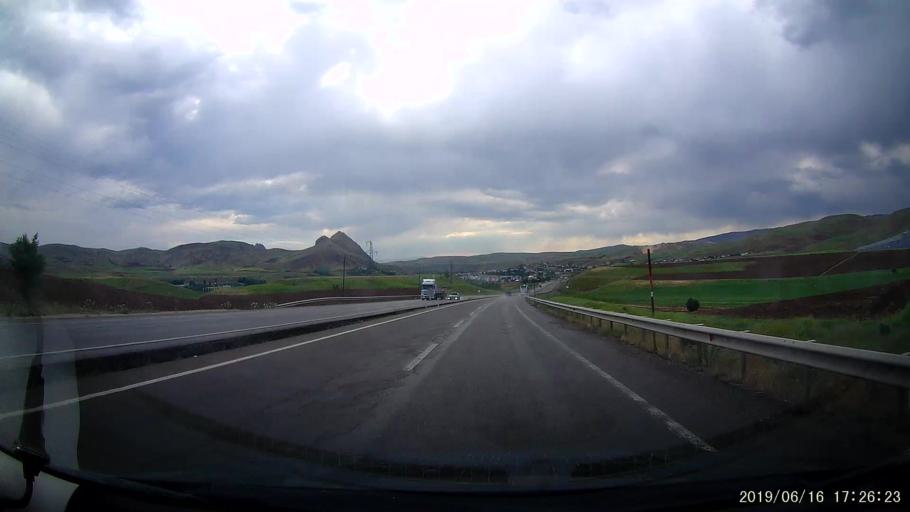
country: TR
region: Erzincan
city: Tercan
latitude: 39.7673
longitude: 40.4137
